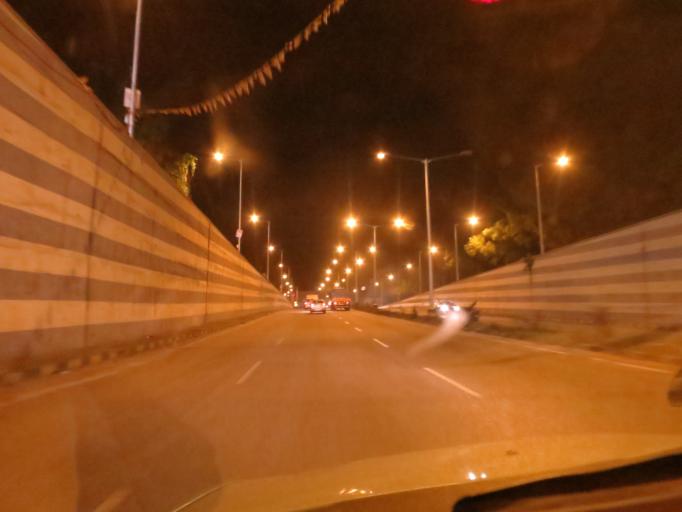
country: IN
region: Karnataka
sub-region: Bangalore Urban
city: Bangalore
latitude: 13.0135
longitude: 77.6622
